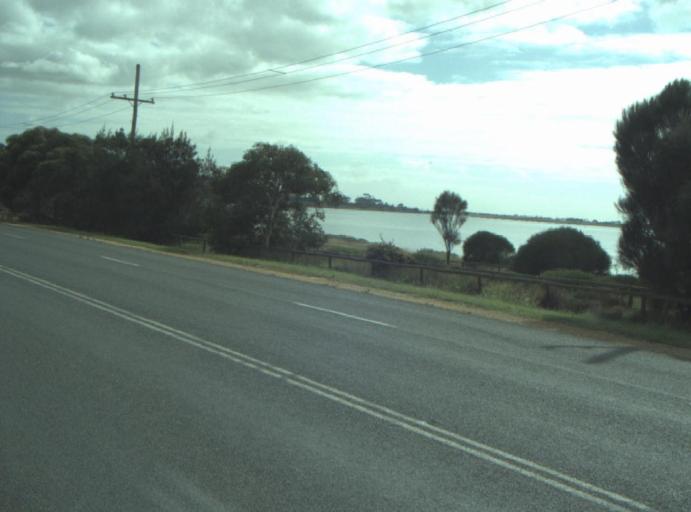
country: AU
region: Victoria
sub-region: Greater Geelong
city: Bell Park
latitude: -38.0812
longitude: 144.3843
